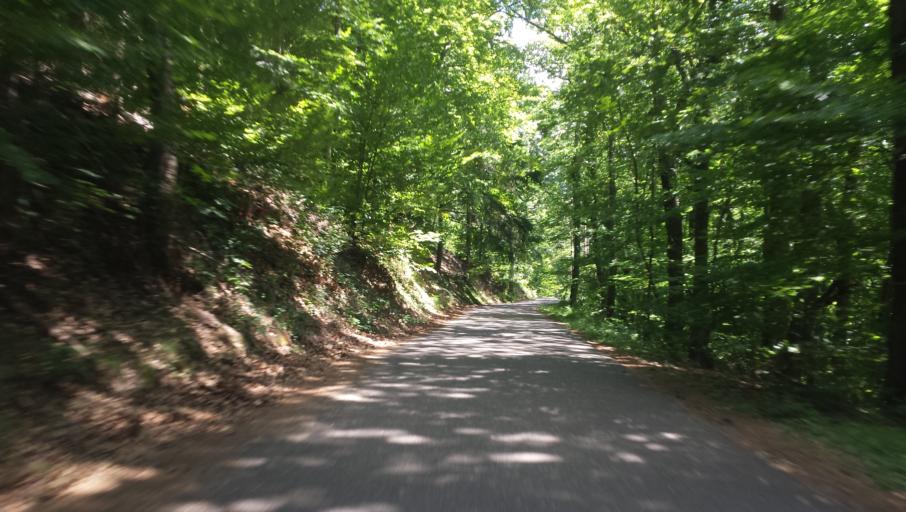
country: DE
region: Rheinland-Pfalz
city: Eschbach
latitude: 49.1761
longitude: 8.0048
